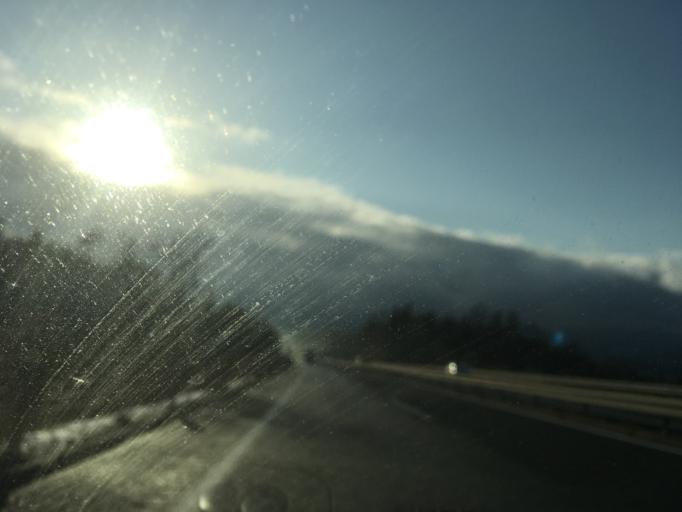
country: JP
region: Miyagi
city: Okawara
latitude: 38.1640
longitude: 140.6601
